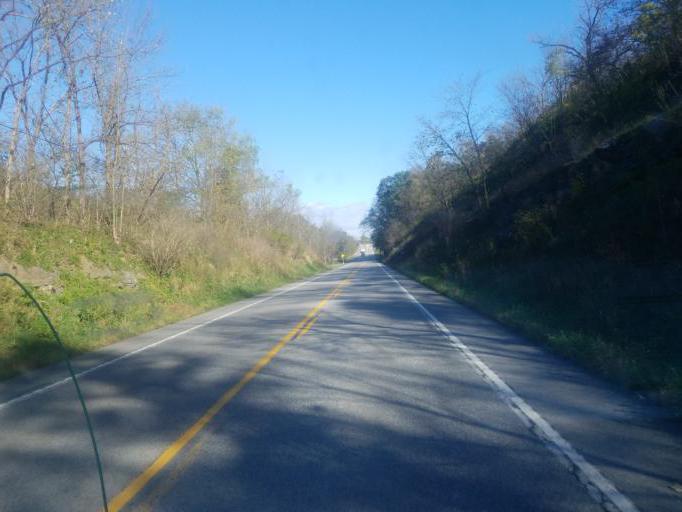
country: US
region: Pennsylvania
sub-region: Blair County
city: Claysburg
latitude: 40.2658
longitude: -78.4602
